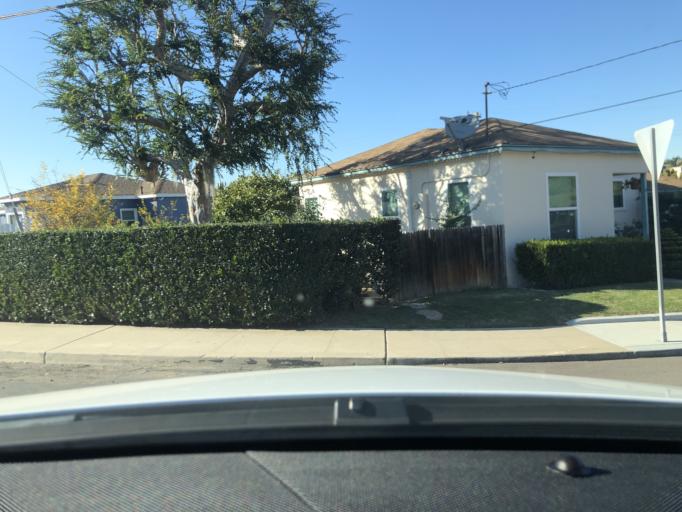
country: US
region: California
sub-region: San Diego County
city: Lemon Grove
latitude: 32.7571
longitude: -117.0686
